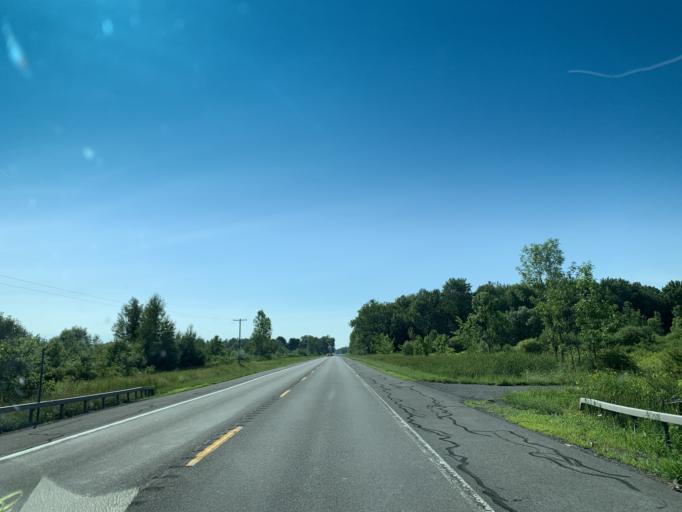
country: US
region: New York
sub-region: Madison County
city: Oneida
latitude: 43.1391
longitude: -75.6244
